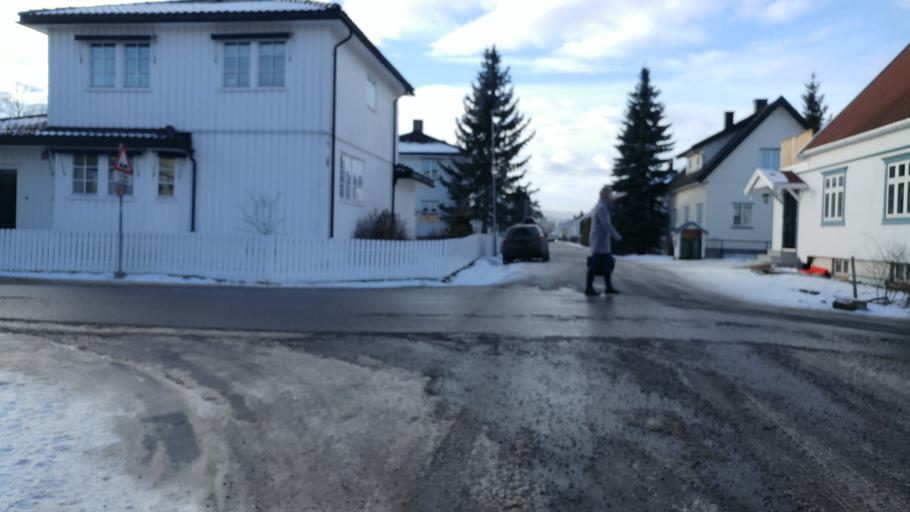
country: NO
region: Akershus
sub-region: Skedsmo
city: Lillestrom
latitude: 59.9590
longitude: 11.0436
